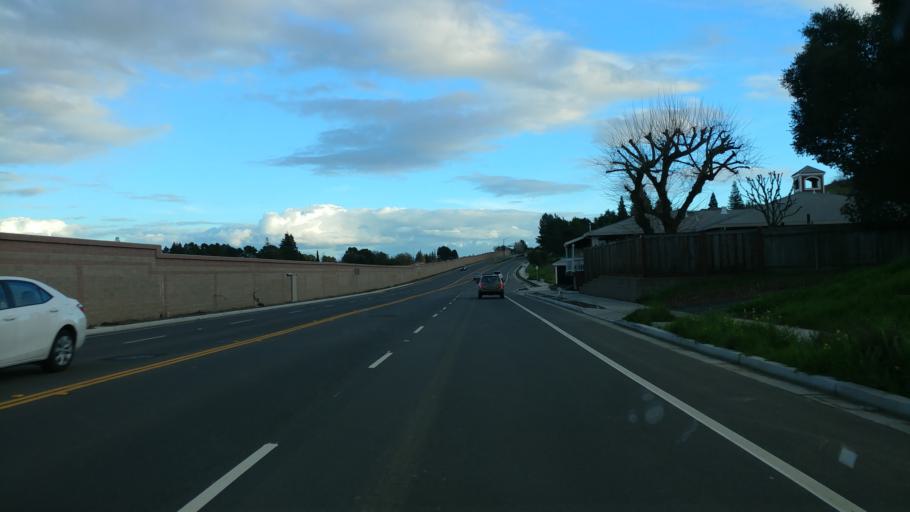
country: US
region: California
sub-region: Contra Costa County
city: San Ramon
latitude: 37.7972
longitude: -121.9865
